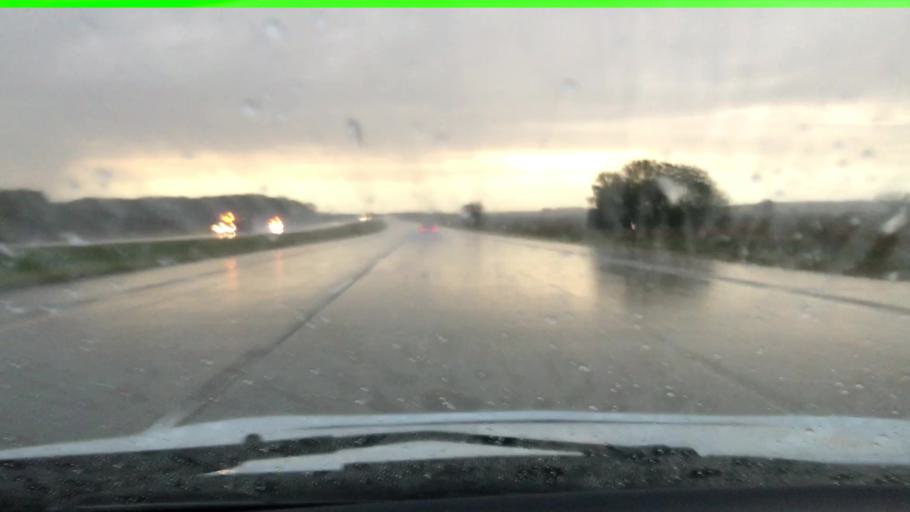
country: US
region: Nebraska
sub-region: Lancaster County
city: Waverly
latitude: 40.8967
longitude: -96.6003
